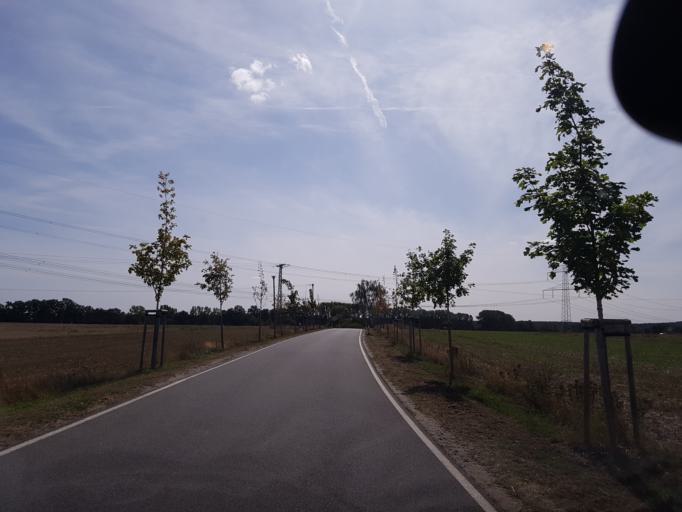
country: DE
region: Brandenburg
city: Luckau
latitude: 51.8540
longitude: 13.6331
